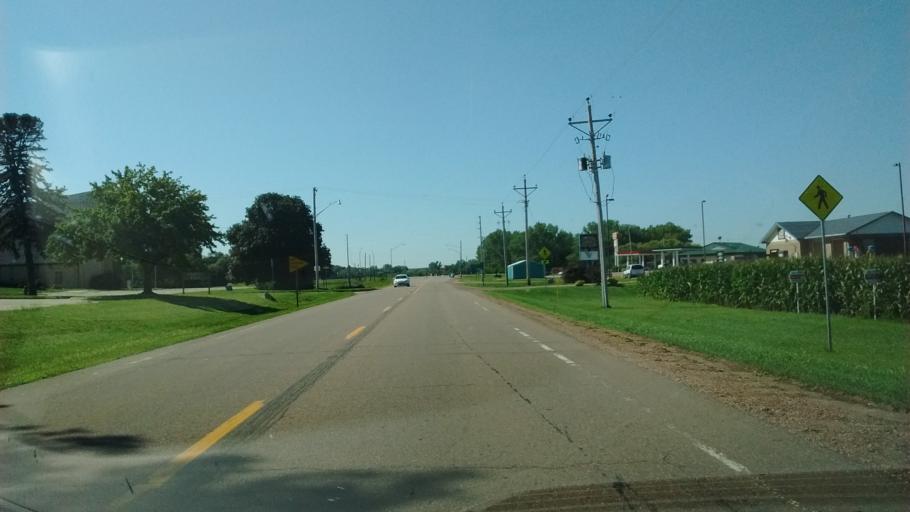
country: US
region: Iowa
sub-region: Woodbury County
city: Moville
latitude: 42.4849
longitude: -96.0758
